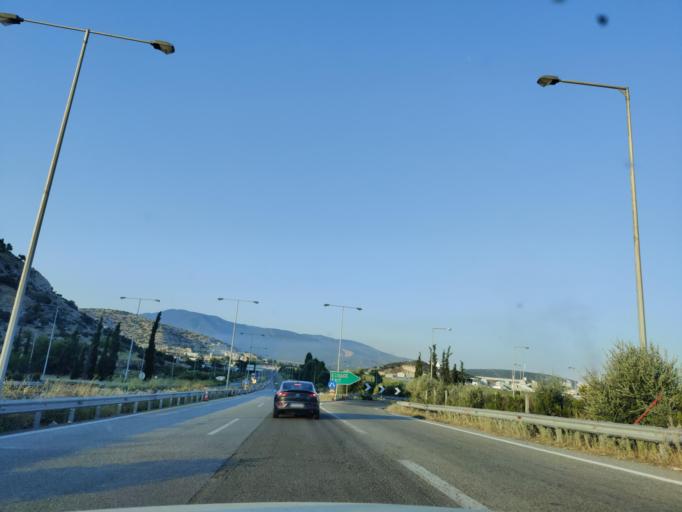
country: GR
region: East Macedonia and Thrace
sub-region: Nomos Kavalas
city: Nea Karvali
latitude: 40.9552
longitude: 24.4636
